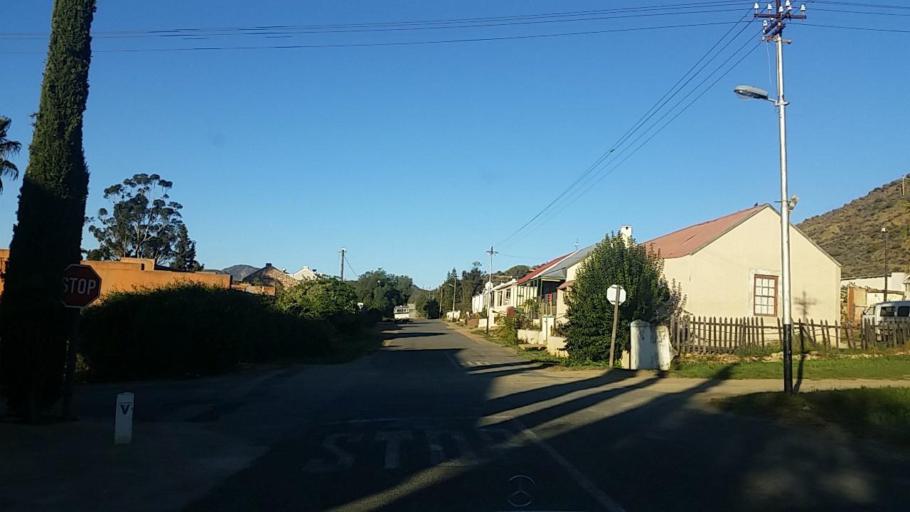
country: ZA
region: Western Cape
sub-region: Eden District Municipality
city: Knysna
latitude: -33.6574
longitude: 23.1277
